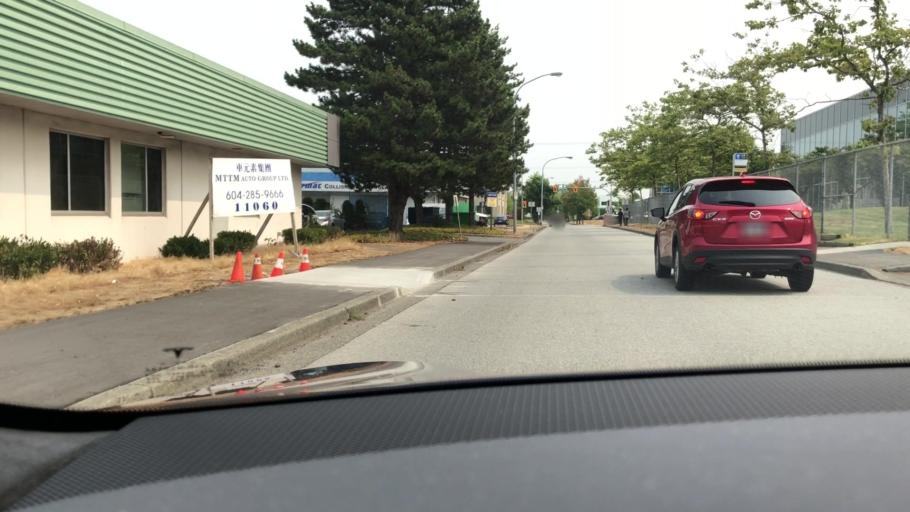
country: CA
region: British Columbia
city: Ladner
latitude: 49.1304
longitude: -123.0940
